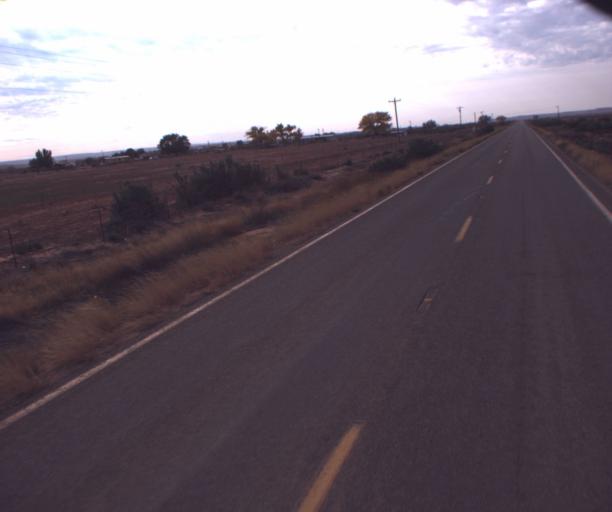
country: US
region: Arizona
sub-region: Apache County
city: Many Farms
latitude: 36.4127
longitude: -109.6074
